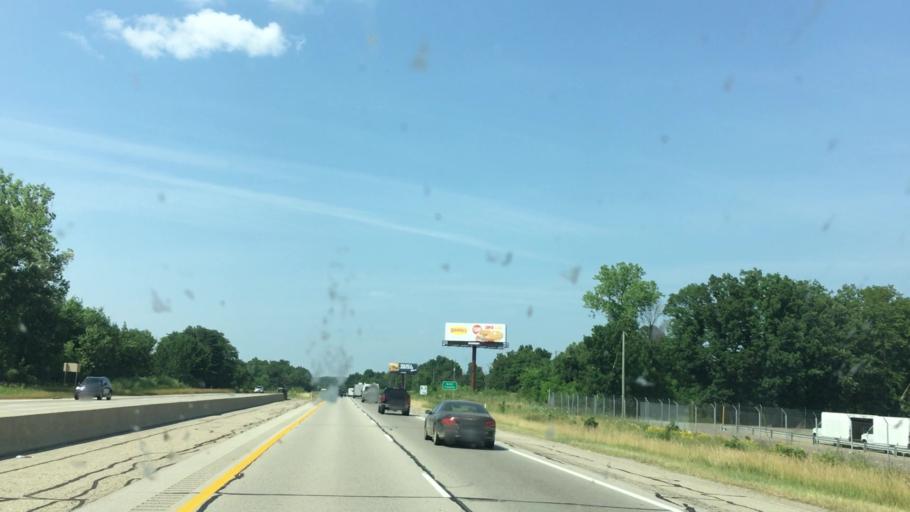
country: US
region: Michigan
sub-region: Kent County
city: Byron Center
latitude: 42.7672
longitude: -85.6721
